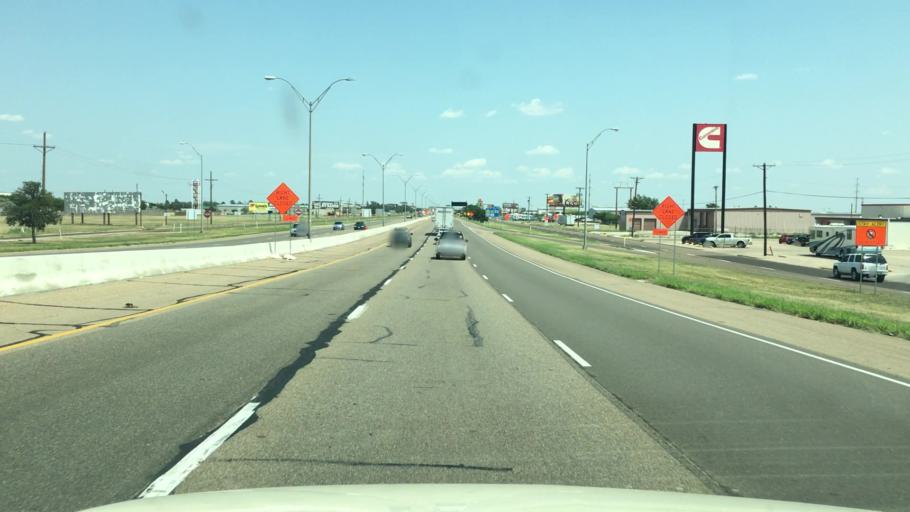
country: US
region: Texas
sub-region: Potter County
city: Amarillo
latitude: 35.1926
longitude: -101.7768
